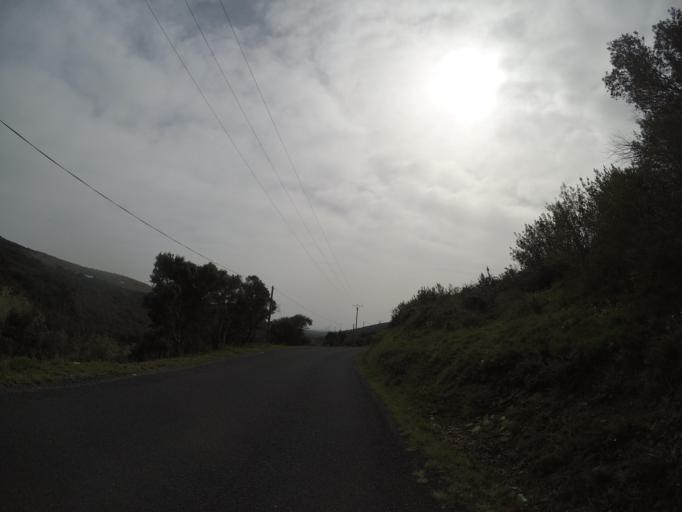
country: FR
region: Languedoc-Roussillon
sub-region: Departement des Pyrenees-Orientales
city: Corneilla-la-Riviere
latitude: 42.7319
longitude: 2.7355
